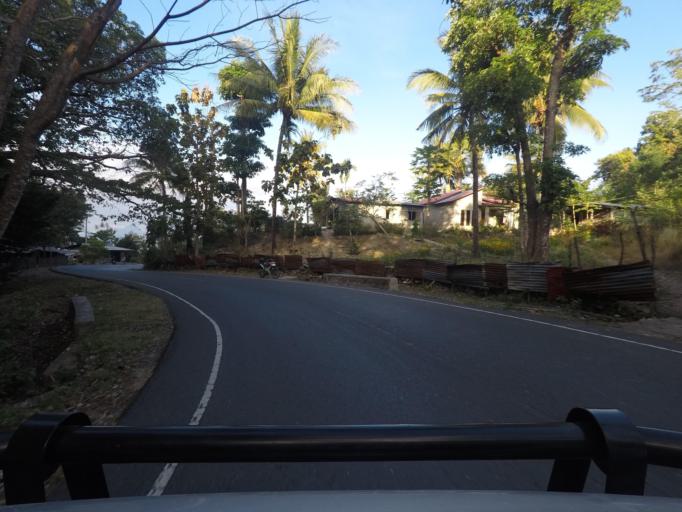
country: TL
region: Bobonaro
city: Maliana
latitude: -8.9533
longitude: 125.0739
